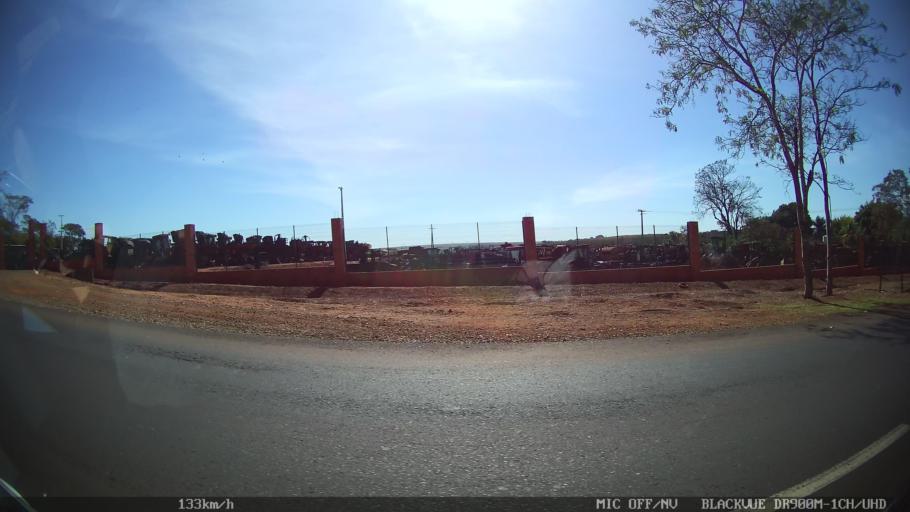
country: BR
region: Sao Paulo
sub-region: Barretos
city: Barretos
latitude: -20.5496
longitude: -48.6318
